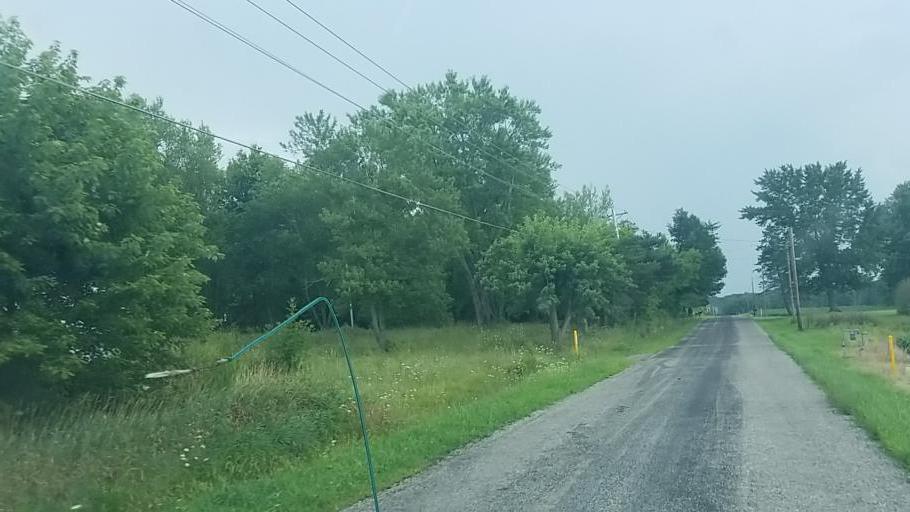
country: US
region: Ohio
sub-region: Medina County
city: Lodi
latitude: 40.9942
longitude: -82.0058
